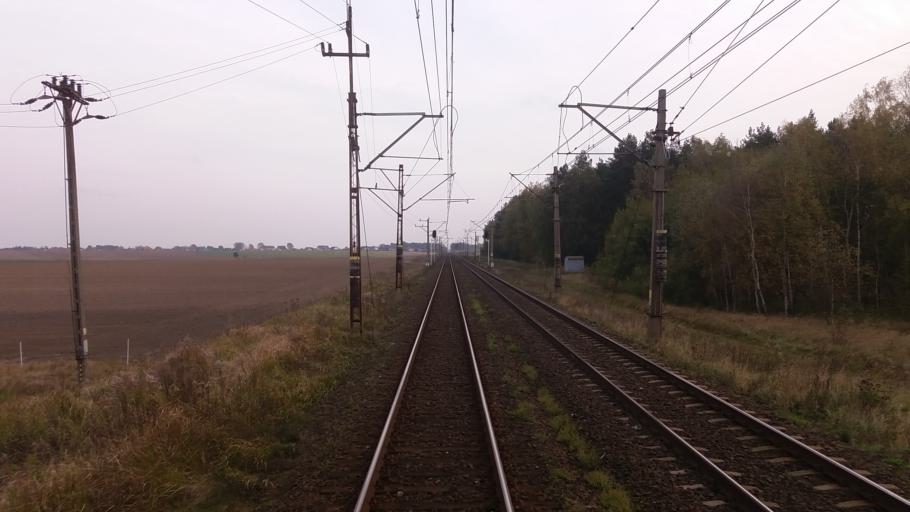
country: PL
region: West Pomeranian Voivodeship
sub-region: Powiat stargardzki
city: Kobylanka
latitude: 53.3618
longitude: 14.9464
